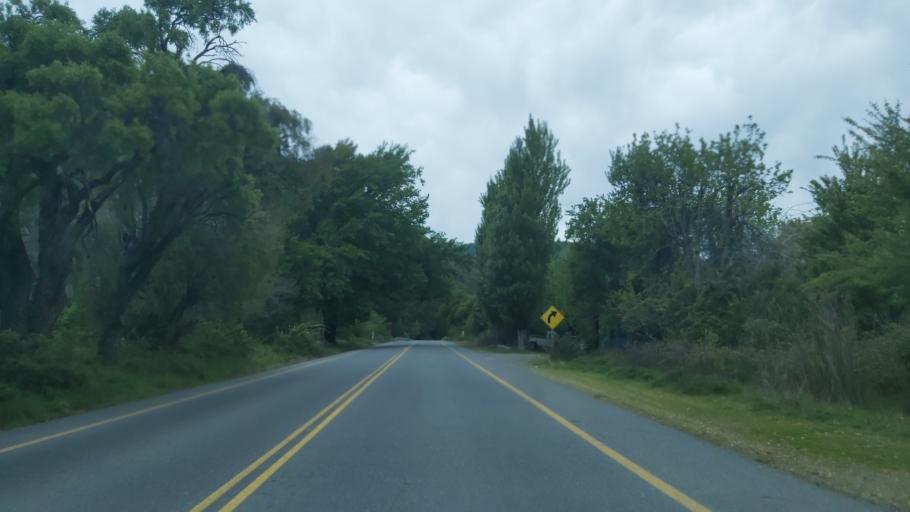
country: CL
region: Maule
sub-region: Provincia de Linares
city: Colbun
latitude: -35.7141
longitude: -71.0472
